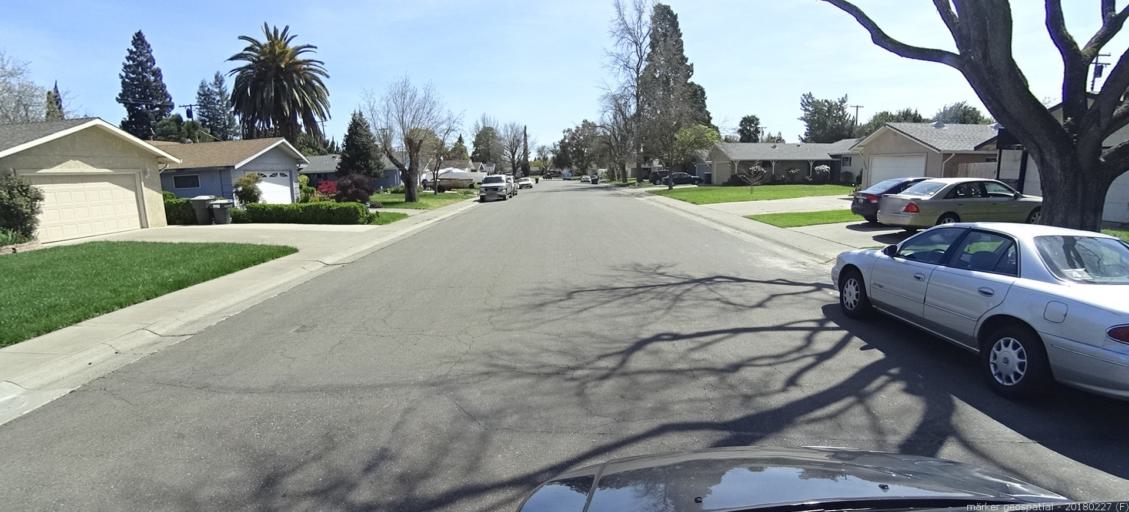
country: US
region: California
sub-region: Sacramento County
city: Rosemont
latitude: 38.5530
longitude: -121.3621
